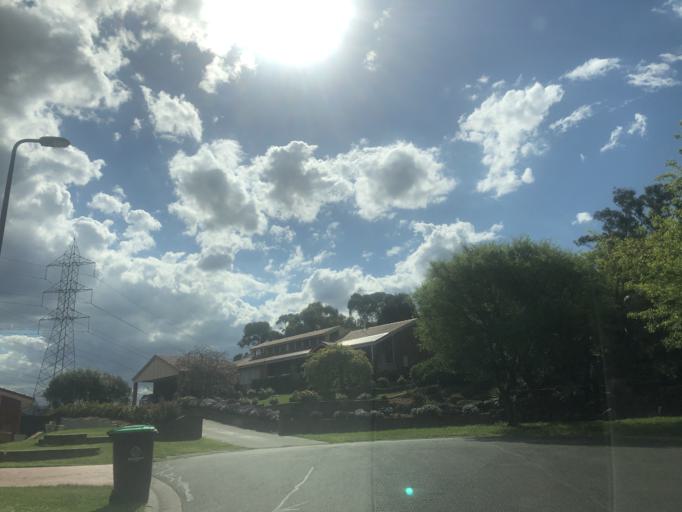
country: AU
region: Victoria
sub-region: Casey
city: Endeavour Hills
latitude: -37.9622
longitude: 145.2738
